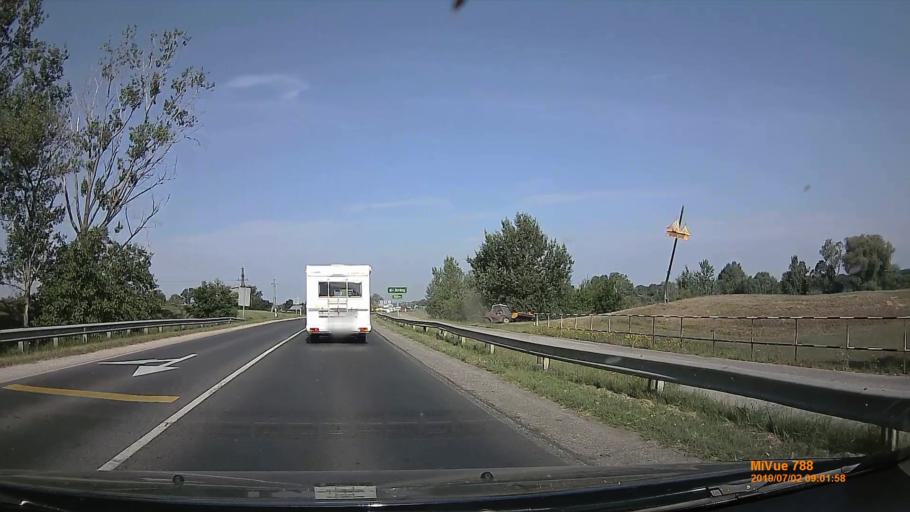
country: HU
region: Gyor-Moson-Sopron
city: Gyor
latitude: 47.6766
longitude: 17.5930
